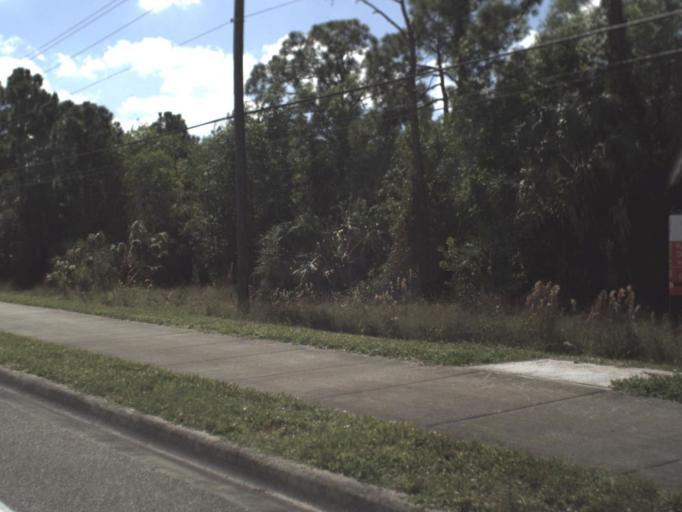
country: US
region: Florida
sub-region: Lee County
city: Villas
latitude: 26.5088
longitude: -81.8609
